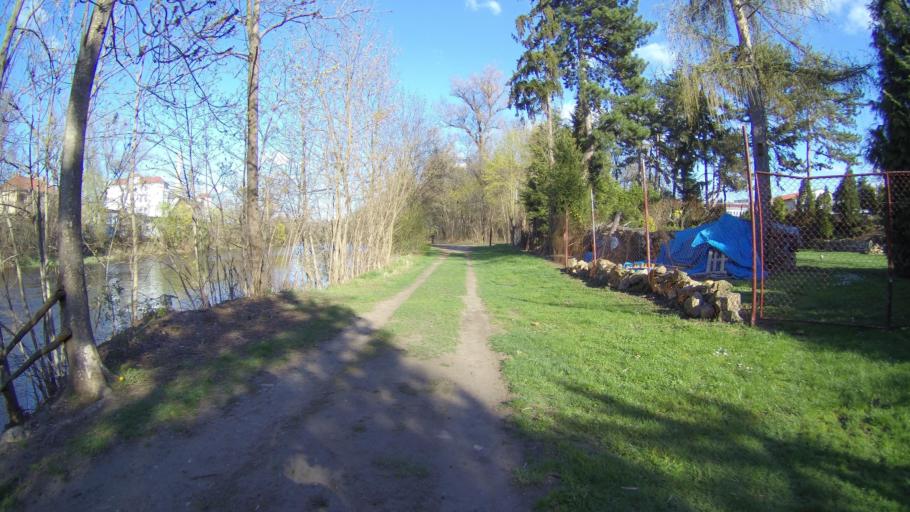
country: CZ
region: Ustecky
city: Zatec
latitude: 50.3326
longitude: 13.5534
